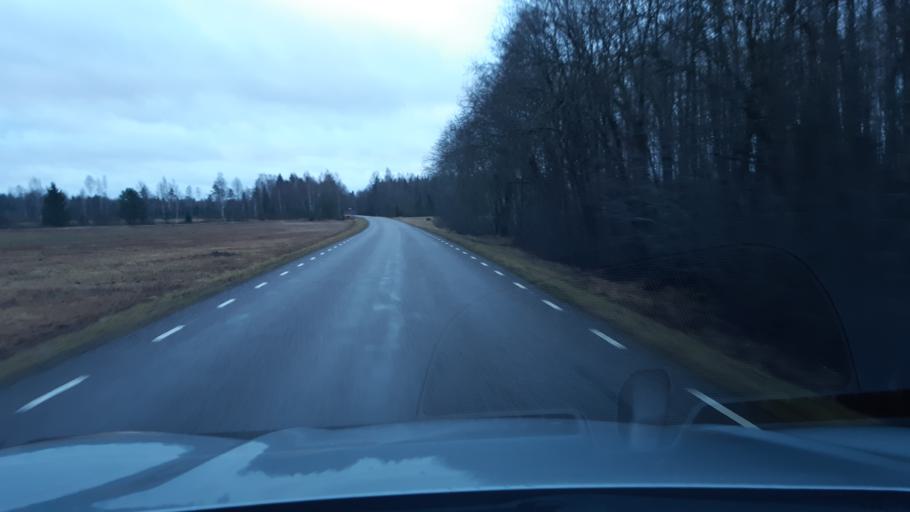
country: EE
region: Raplamaa
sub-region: Kohila vald
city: Kohila
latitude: 59.0882
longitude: 24.6743
